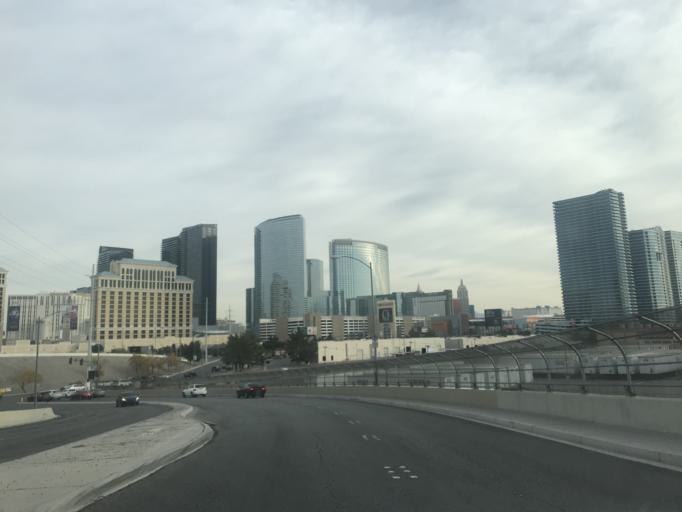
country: US
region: Nevada
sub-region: Clark County
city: Paradise
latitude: 36.1138
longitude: -115.1847
